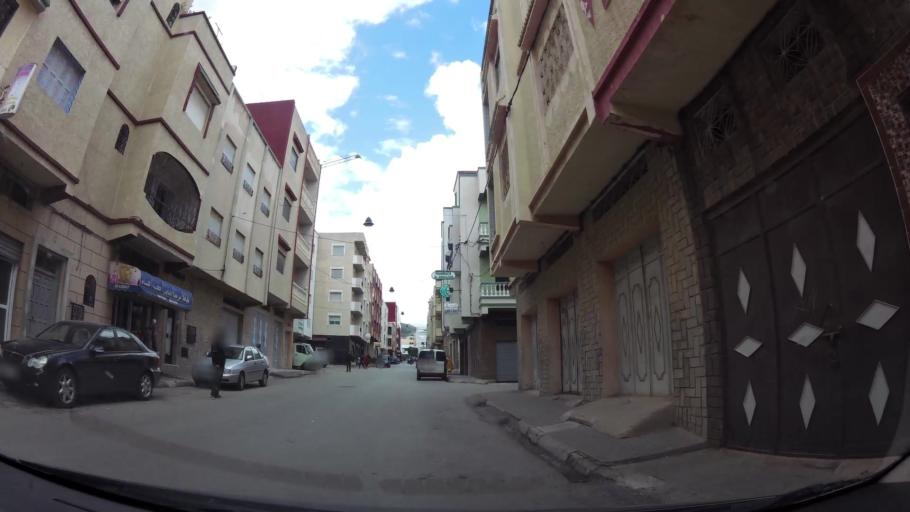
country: MA
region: Tanger-Tetouan
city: Tetouan
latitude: 35.5775
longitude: -5.3541
